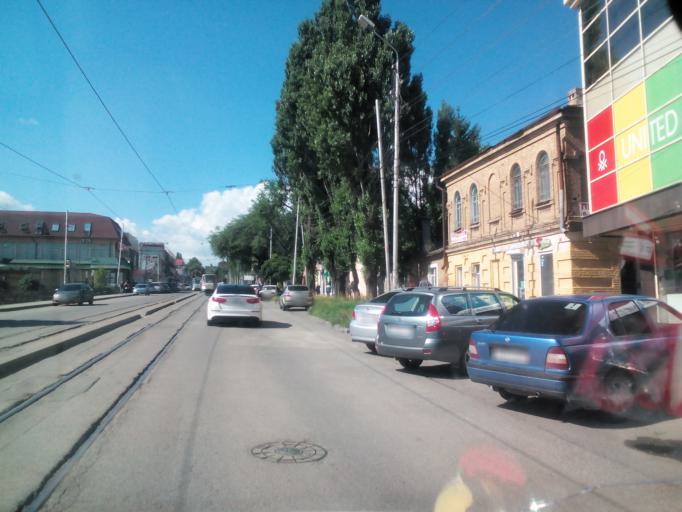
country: RU
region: Stavropol'skiy
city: Pyatigorsk
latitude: 44.0401
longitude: 43.0644
